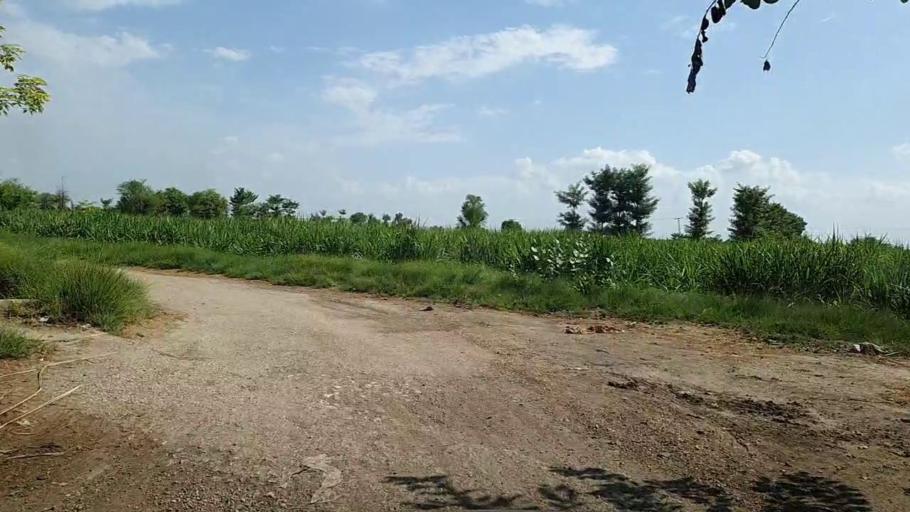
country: PK
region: Sindh
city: Bhiria
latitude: 26.9058
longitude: 68.2249
